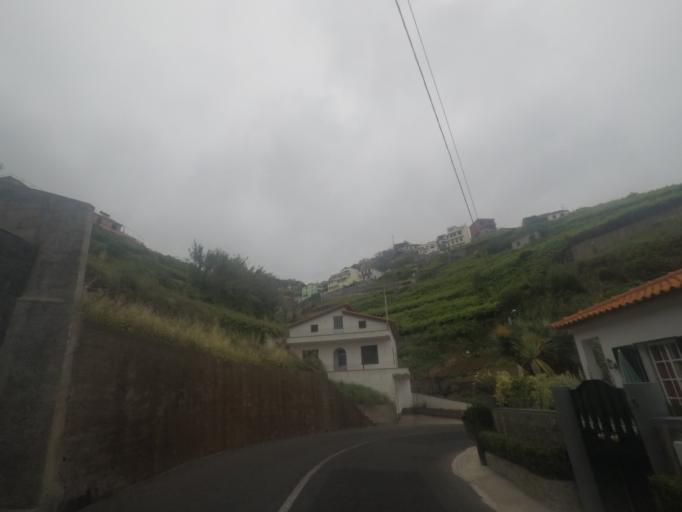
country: PT
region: Madeira
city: Camara de Lobos
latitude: 32.6731
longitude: -16.9713
